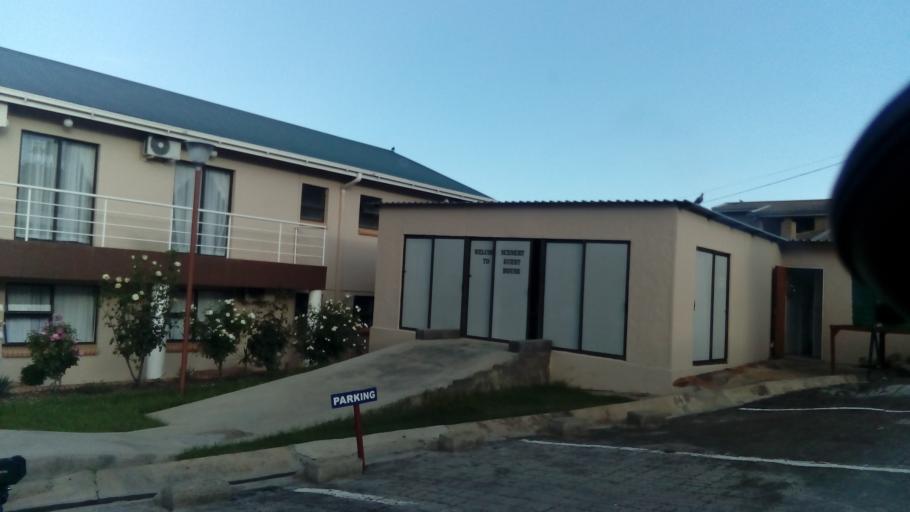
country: LS
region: Maseru
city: Maseru
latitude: -29.3084
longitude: 27.5021
